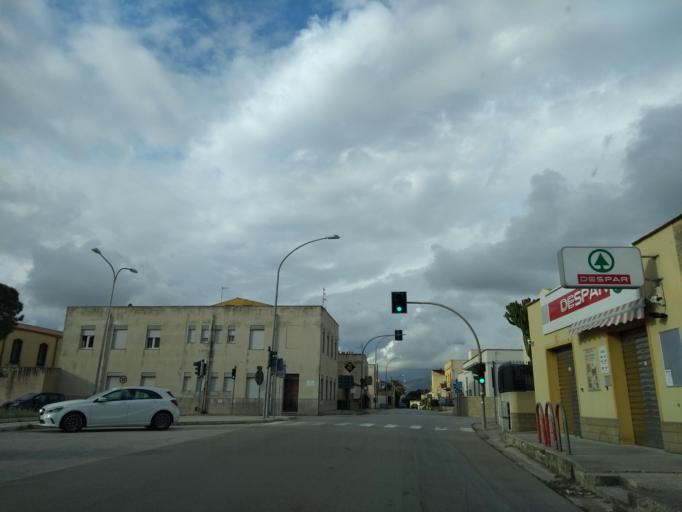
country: IT
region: Sicily
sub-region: Trapani
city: Marausa
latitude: 37.9509
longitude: 12.5141
